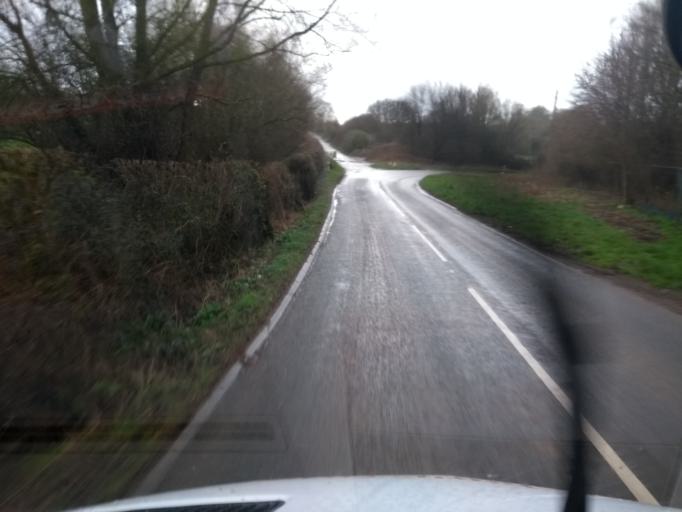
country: GB
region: England
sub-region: Somerset
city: Bruton
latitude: 51.0915
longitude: -2.4646
